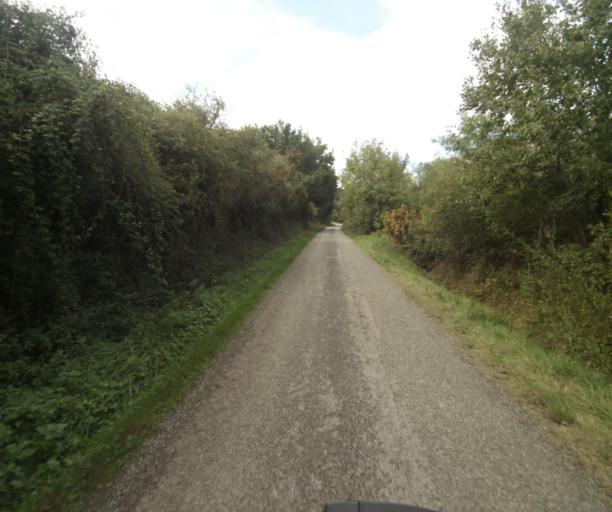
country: FR
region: Midi-Pyrenees
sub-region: Departement du Tarn-et-Garonne
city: Saint-Porquier
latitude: 43.9547
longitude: 1.1506
